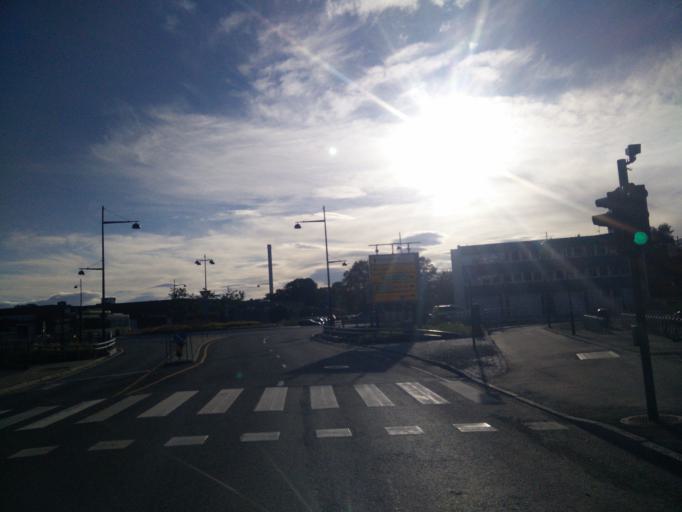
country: NO
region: Sor-Trondelag
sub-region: Trondheim
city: Trondheim
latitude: 63.4363
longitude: 10.4571
